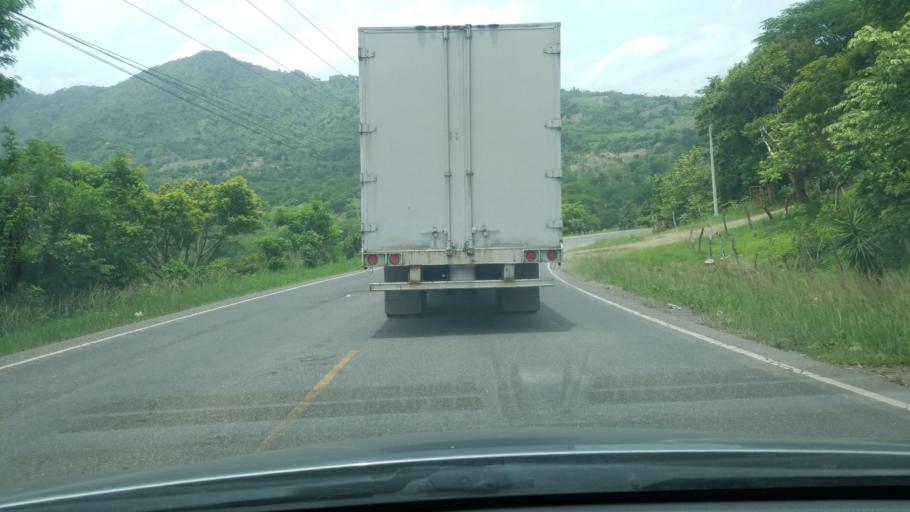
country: HN
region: Copan
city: Ojos de Agua
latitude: 14.7184
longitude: -88.7732
